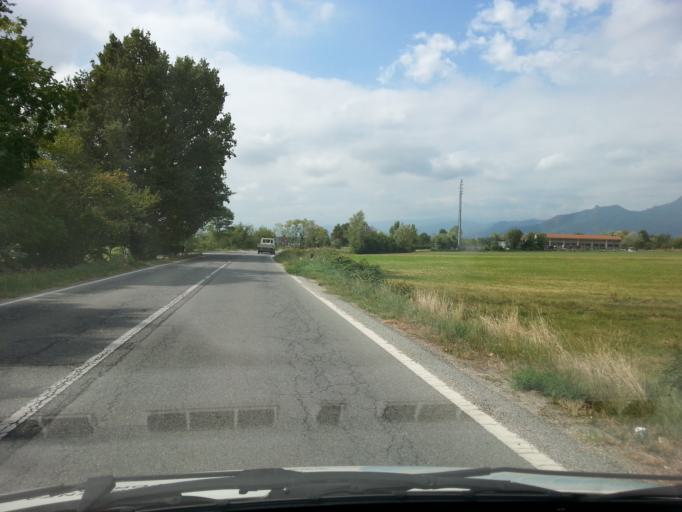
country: IT
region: Piedmont
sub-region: Provincia di Torino
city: Piossasco
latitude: 44.9785
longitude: 7.4518
